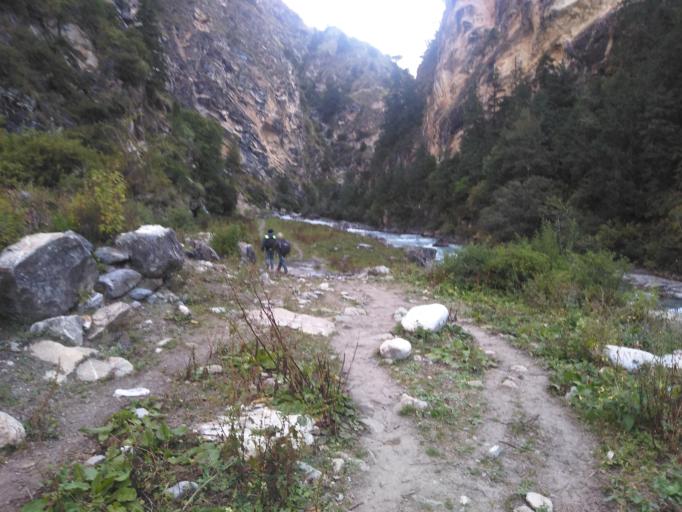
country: NP
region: Western Region
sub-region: Dhawalagiri Zone
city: Jomsom
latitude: 28.9308
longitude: 83.0446
